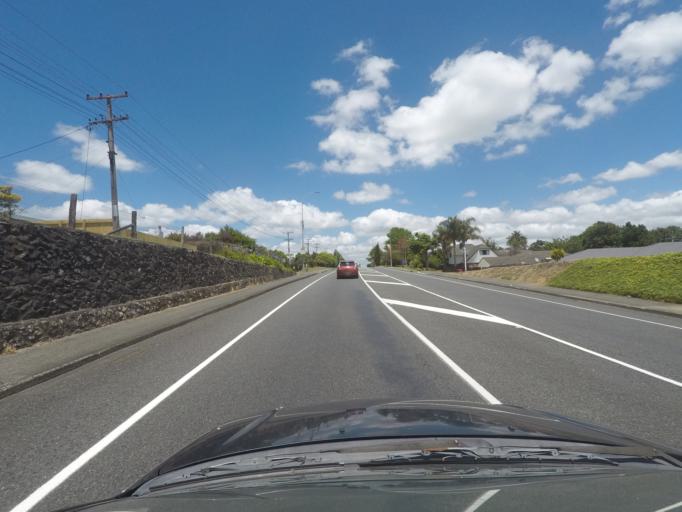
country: NZ
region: Northland
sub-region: Whangarei
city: Whangarei
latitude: -35.7468
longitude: 174.3672
